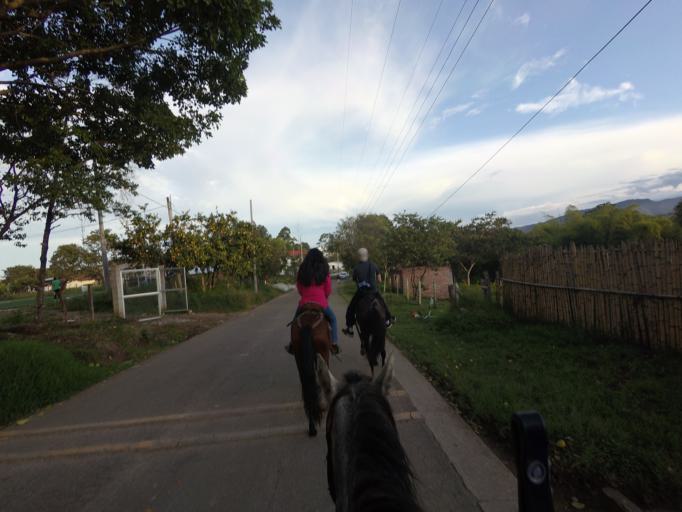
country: CO
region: Huila
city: San Agustin
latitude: 1.8957
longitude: -76.2739
